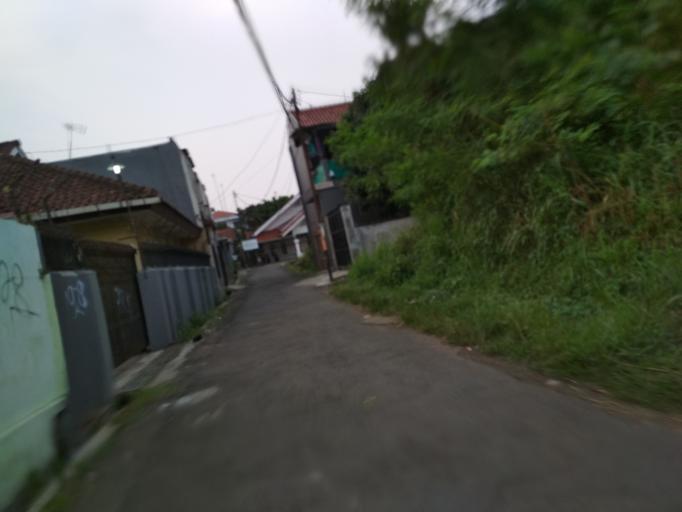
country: ID
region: West Java
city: Ciampea
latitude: -6.5610
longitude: 106.7362
